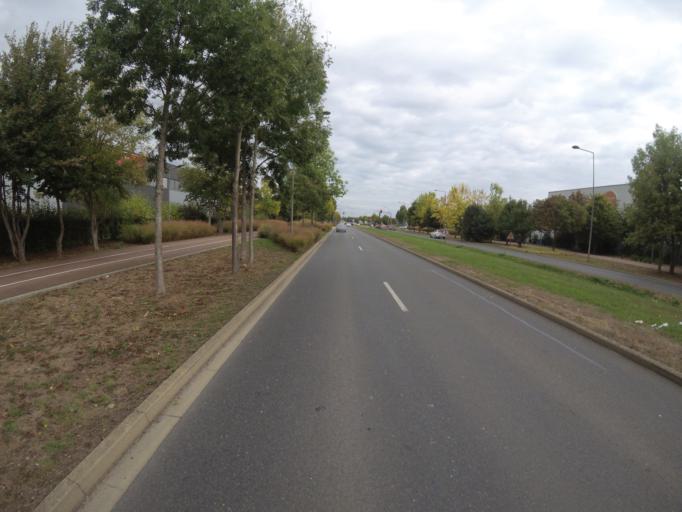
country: FR
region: Ile-de-France
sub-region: Departement de Seine-et-Marne
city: Chanteloup-en-Brie
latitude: 48.8553
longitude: 2.7573
